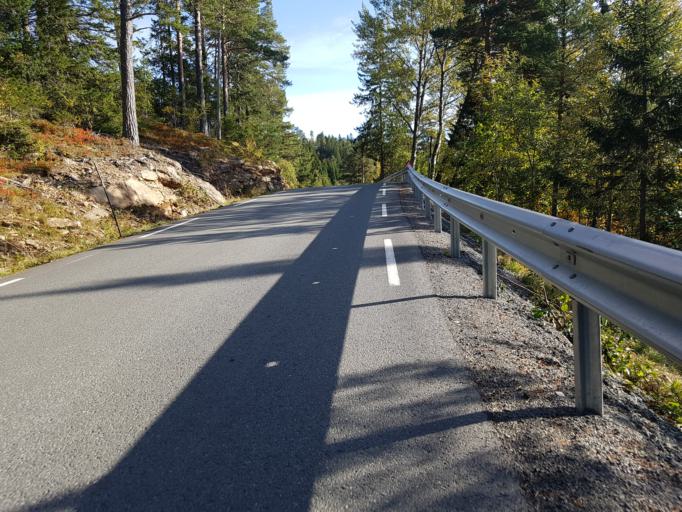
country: NO
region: Sor-Trondelag
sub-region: Malvik
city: Malvik
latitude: 63.3683
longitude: 10.6179
